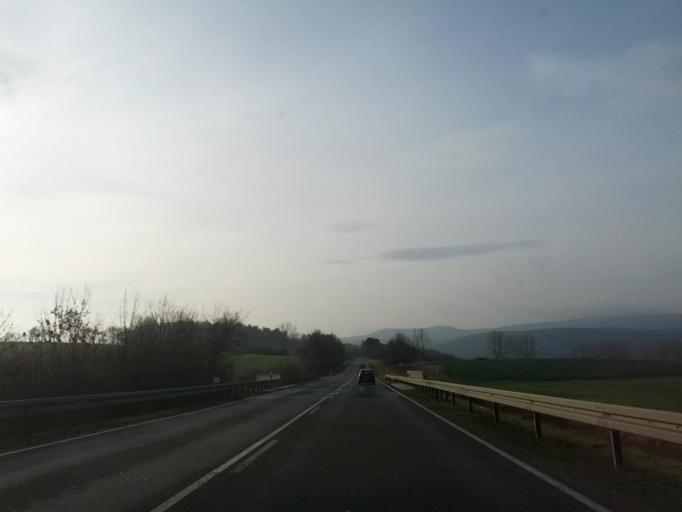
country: DE
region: Thuringia
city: Barchfeld
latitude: 50.7943
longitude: 10.3198
